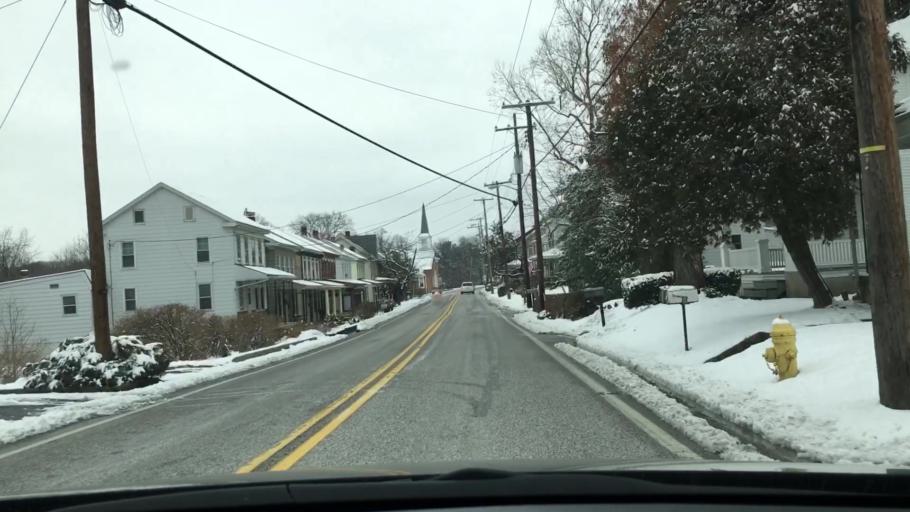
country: US
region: Pennsylvania
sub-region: York County
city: Emigsville
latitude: 40.0022
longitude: -76.7048
